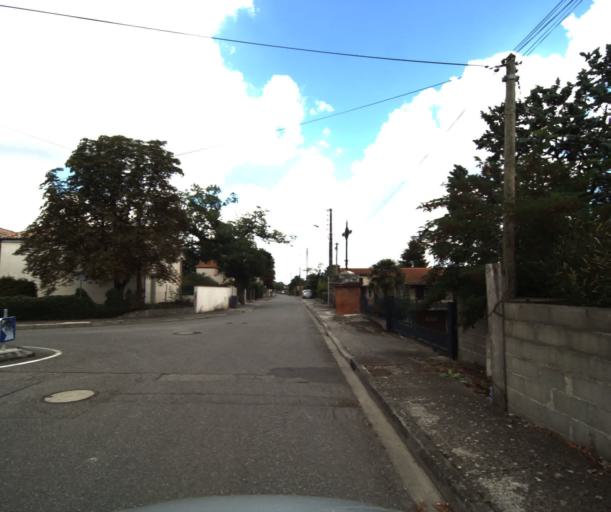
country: FR
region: Midi-Pyrenees
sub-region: Departement de la Haute-Garonne
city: Lacasse
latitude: 43.3960
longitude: 1.2681
